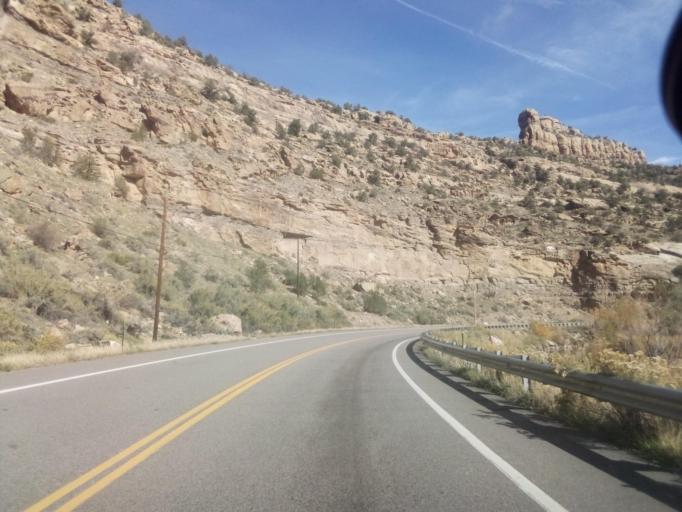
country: US
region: Colorado
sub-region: Mesa County
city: Palisade
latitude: 39.1869
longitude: -108.2651
